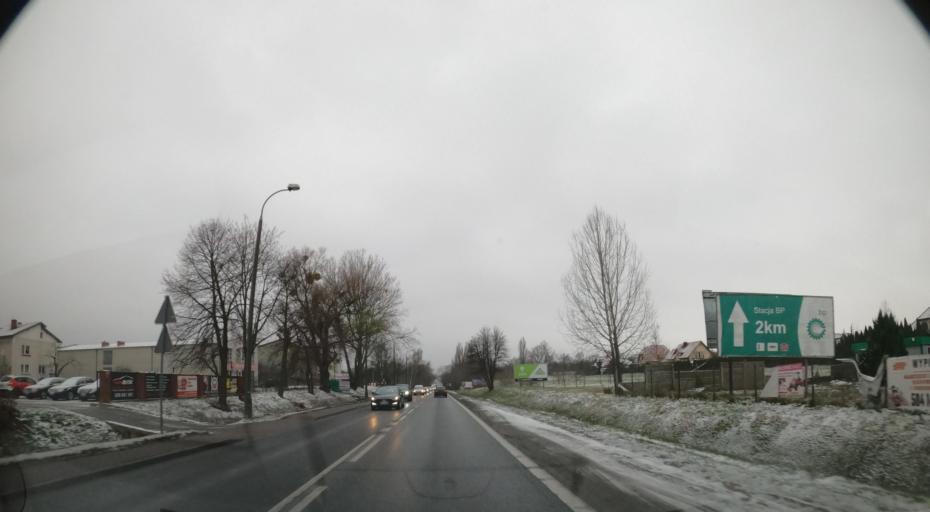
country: PL
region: Masovian Voivodeship
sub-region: Plock
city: Plock
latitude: 52.5326
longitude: 19.7710
